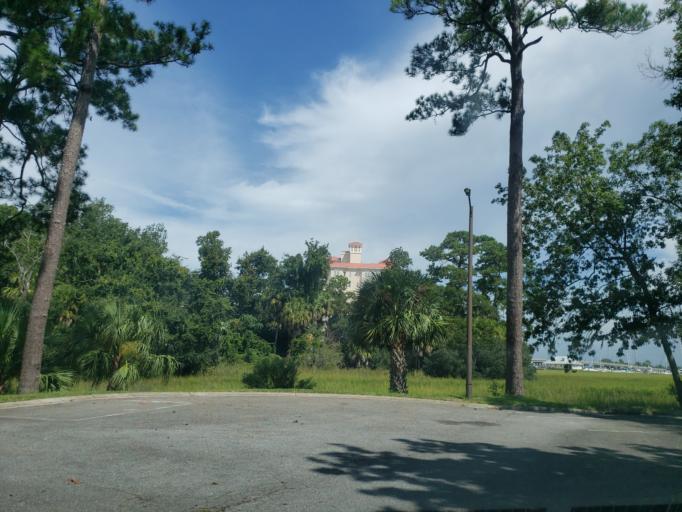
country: US
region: Georgia
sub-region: Chatham County
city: Wilmington Island
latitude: 32.0318
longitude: -80.9605
